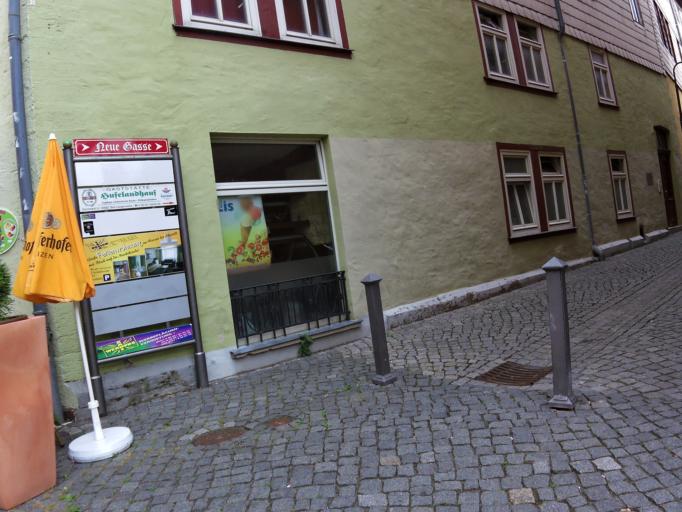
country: DE
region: Thuringia
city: Bad Langensalza
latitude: 51.1082
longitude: 10.6458
